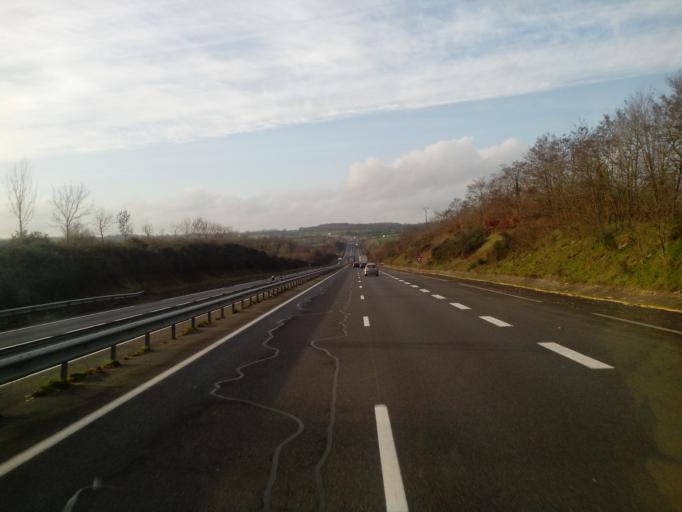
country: FR
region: Poitou-Charentes
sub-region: Departement des Deux-Sevres
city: Bressuire
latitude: 46.8552
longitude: -0.4834
